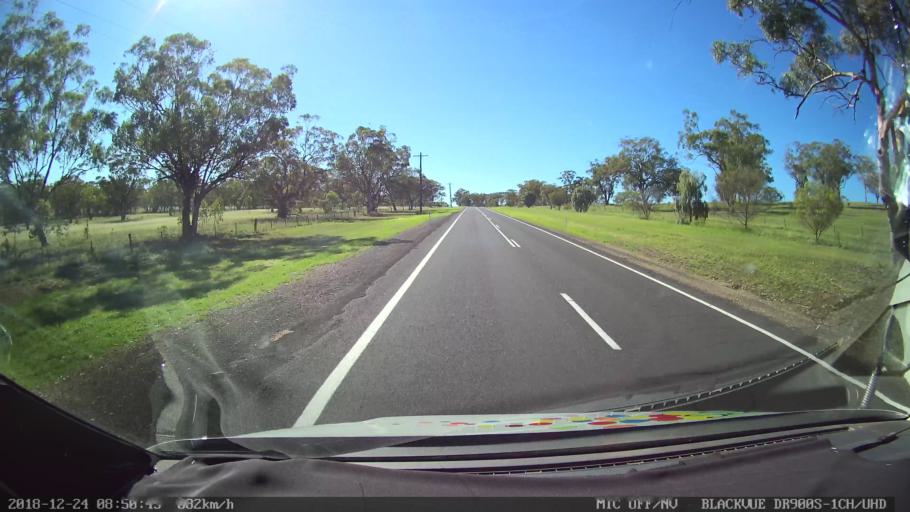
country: AU
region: New South Wales
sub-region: Liverpool Plains
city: Quirindi
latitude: -31.4785
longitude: 150.6682
